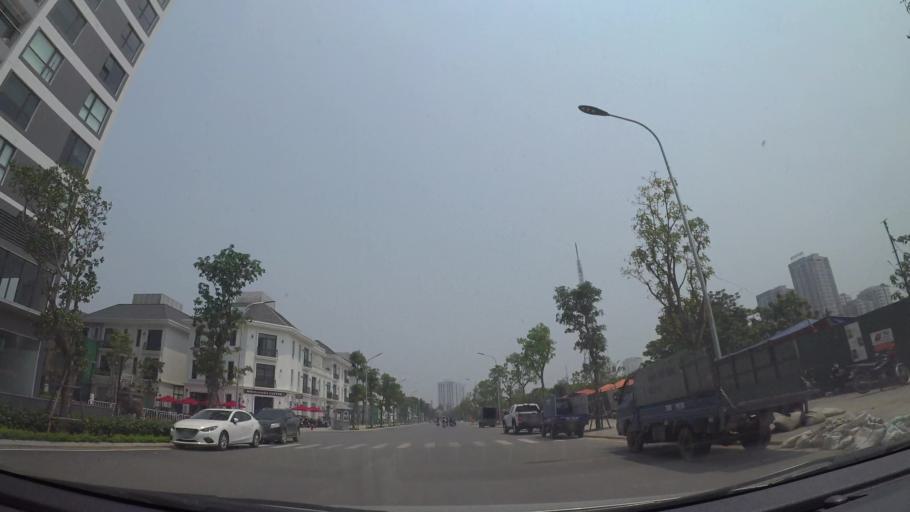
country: VN
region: Ha Noi
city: Thanh Xuan
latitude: 21.0002
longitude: 105.7839
